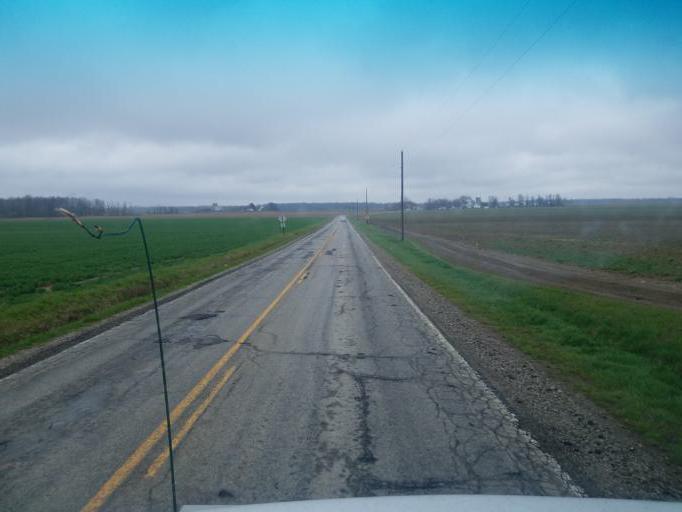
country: US
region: Ohio
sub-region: Huron County
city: Plymouth
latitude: 40.9436
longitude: -82.6447
